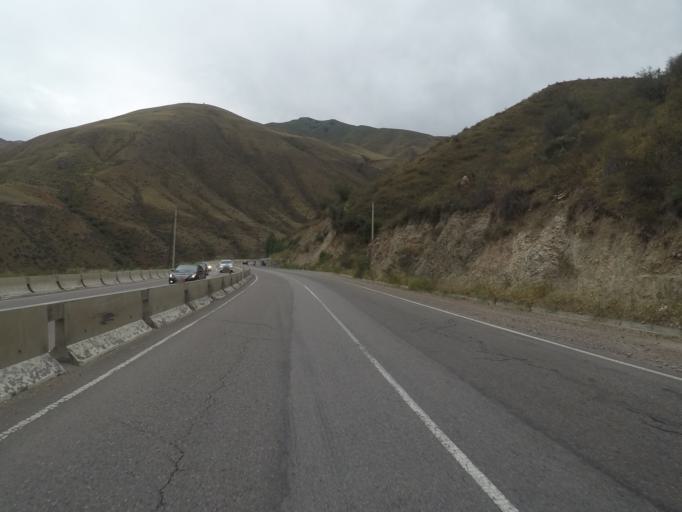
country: KG
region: Chuy
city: Bystrovka
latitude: 42.6607
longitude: 75.8852
